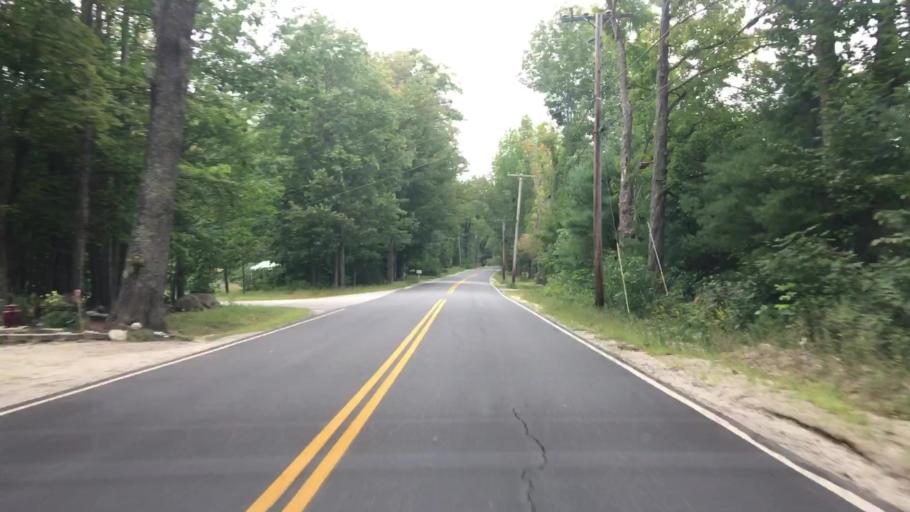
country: US
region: Maine
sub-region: Cumberland County
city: New Gloucester
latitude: 43.9112
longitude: -70.2505
